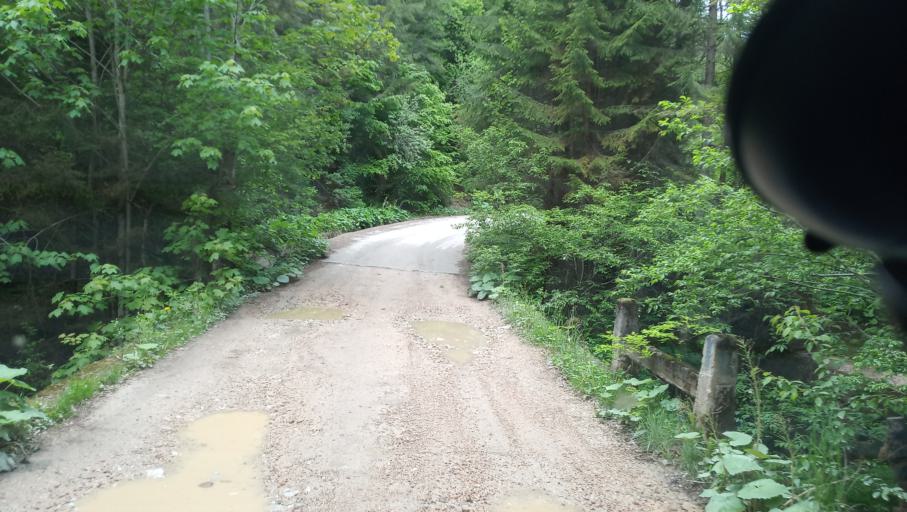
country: RO
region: Alba
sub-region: Comuna Scarisoara
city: Scarisoara
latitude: 46.4874
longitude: 22.8438
